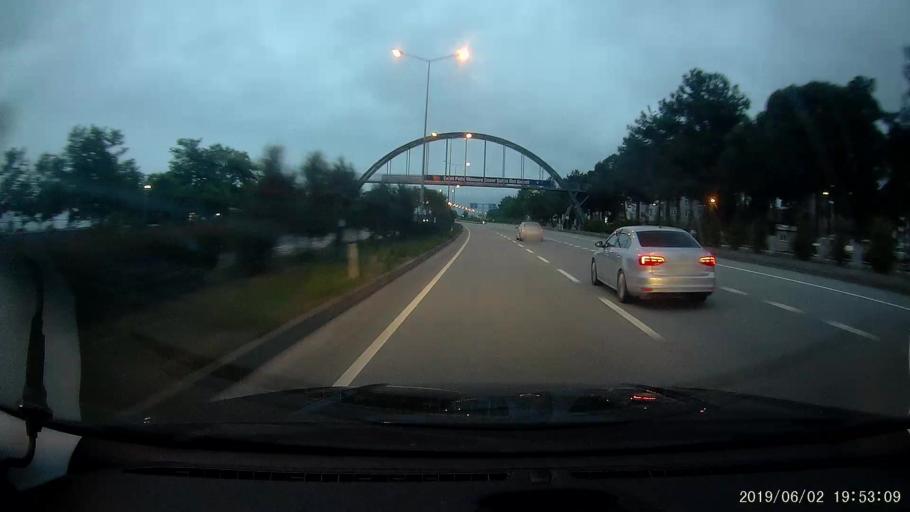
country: TR
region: Trabzon
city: Espiye
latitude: 40.9482
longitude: 38.6995
